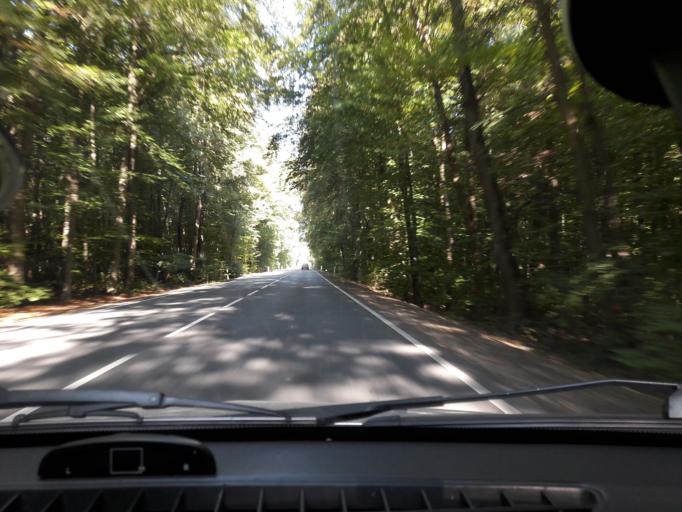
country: DE
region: Hesse
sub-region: Regierungsbezirk Darmstadt
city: Wiesbaden
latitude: 50.0962
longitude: 8.2086
